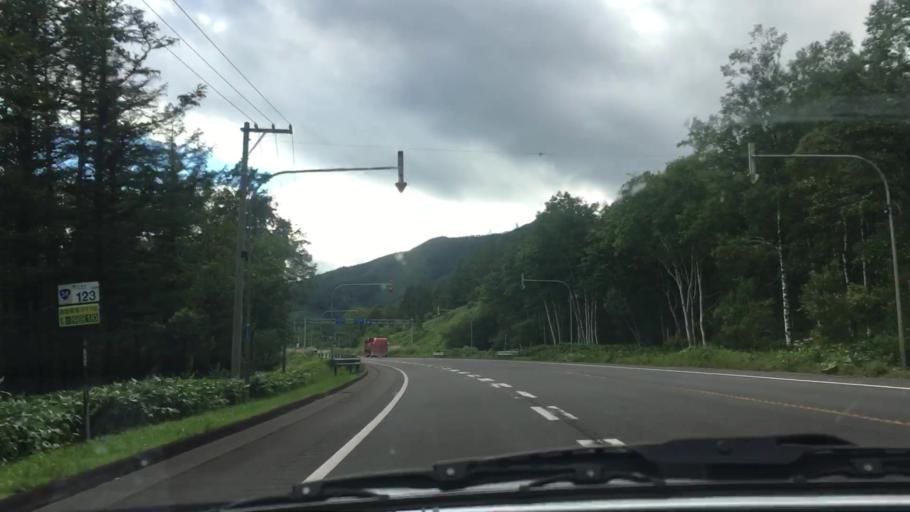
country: JP
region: Hokkaido
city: Otofuke
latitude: 43.1596
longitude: 142.7907
